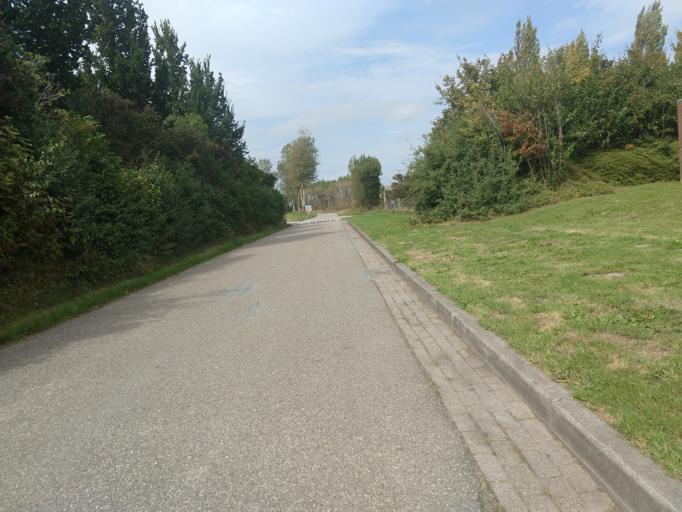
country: NL
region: Zeeland
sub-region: Gemeente Reimerswaal
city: Yerseke
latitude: 51.4523
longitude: 4.0016
